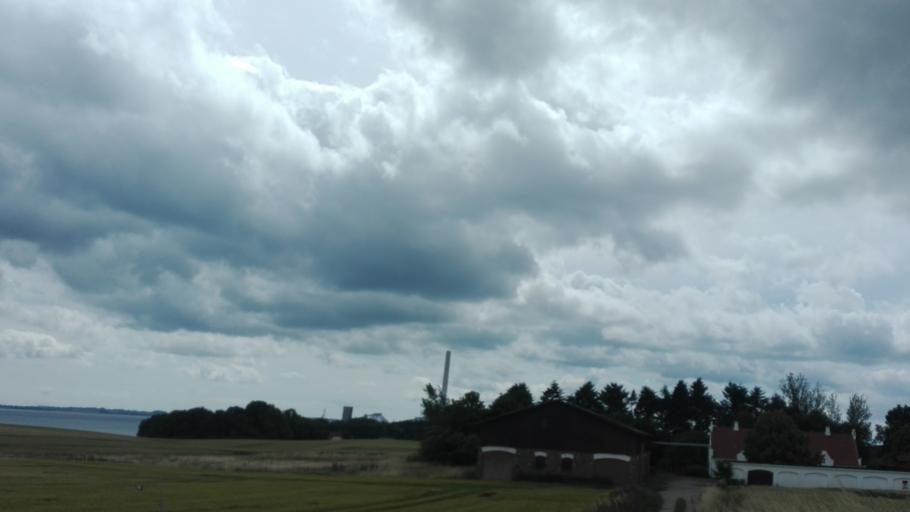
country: DK
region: Central Jutland
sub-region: Arhus Kommune
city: Logten
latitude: 56.2662
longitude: 10.3397
